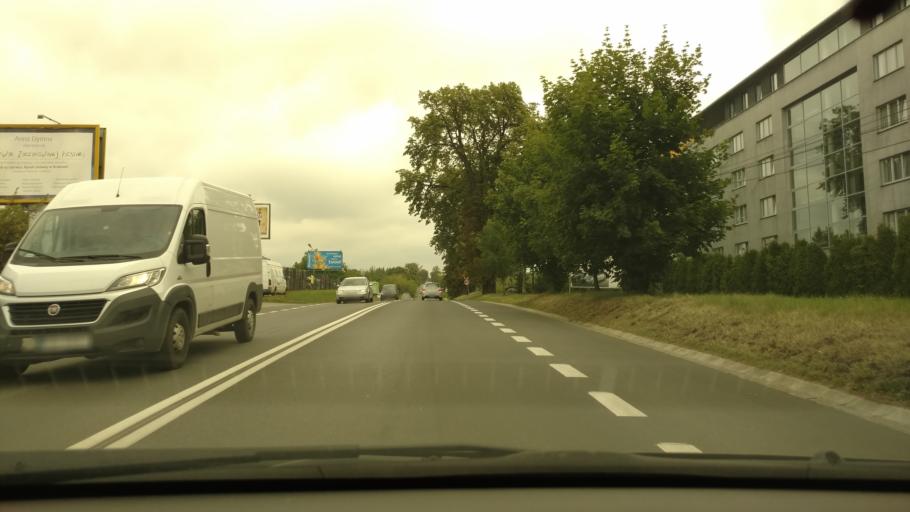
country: PL
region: Lesser Poland Voivodeship
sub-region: Krakow
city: Krakow
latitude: 50.0995
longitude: 19.9628
